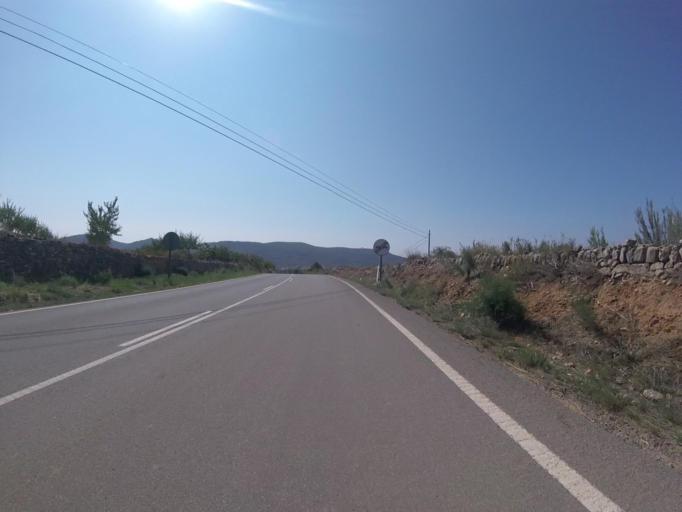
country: ES
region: Valencia
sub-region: Provincia de Castello
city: Adzaneta
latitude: 40.2305
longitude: -0.1764
